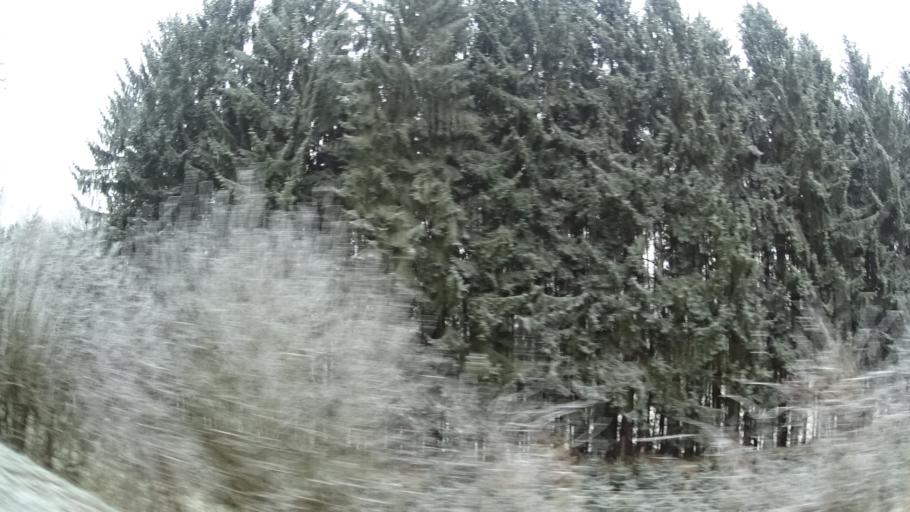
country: DE
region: Hesse
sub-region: Regierungsbezirk Darmstadt
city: Steinau an der Strasse
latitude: 50.2541
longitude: 9.5057
